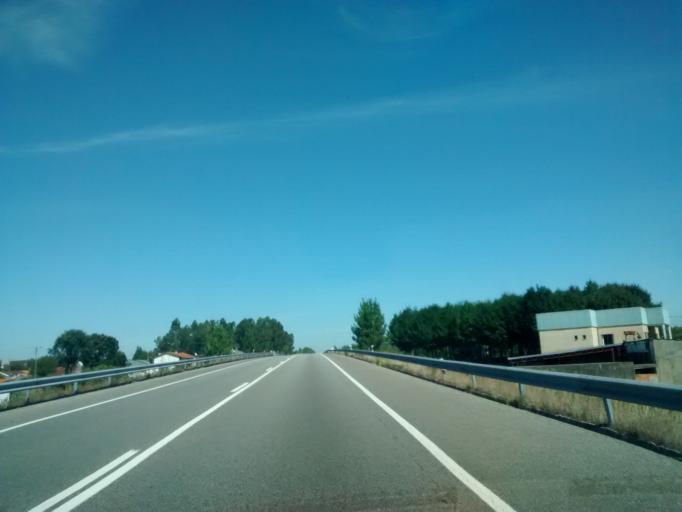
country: PT
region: Aveiro
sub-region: Anadia
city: Sangalhos
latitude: 40.4737
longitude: -8.4718
